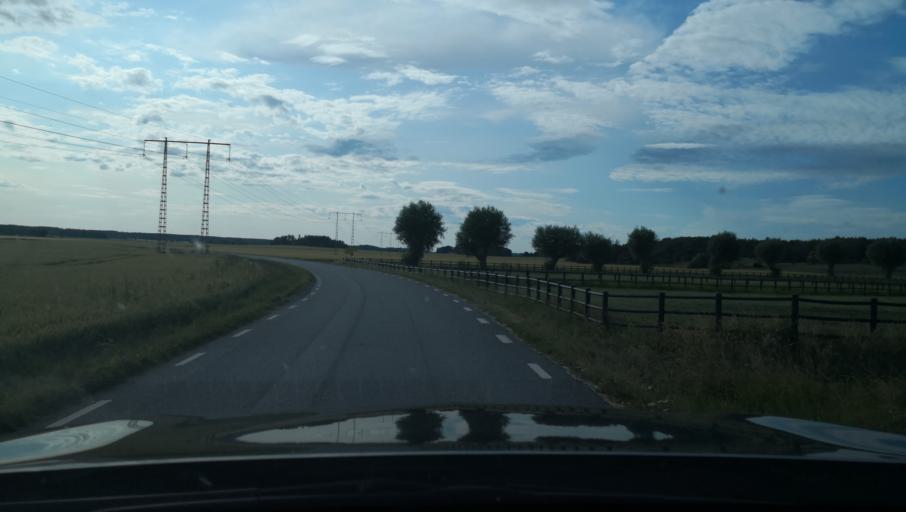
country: SE
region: Uppsala
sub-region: Enkopings Kommun
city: Orsundsbro
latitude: 59.6995
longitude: 17.3078
